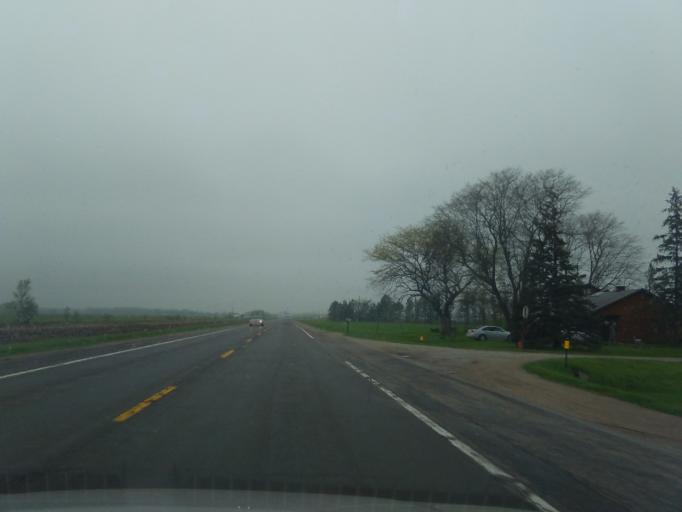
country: US
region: Nebraska
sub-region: Cuming County
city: West Point
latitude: 41.9144
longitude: -96.7872
